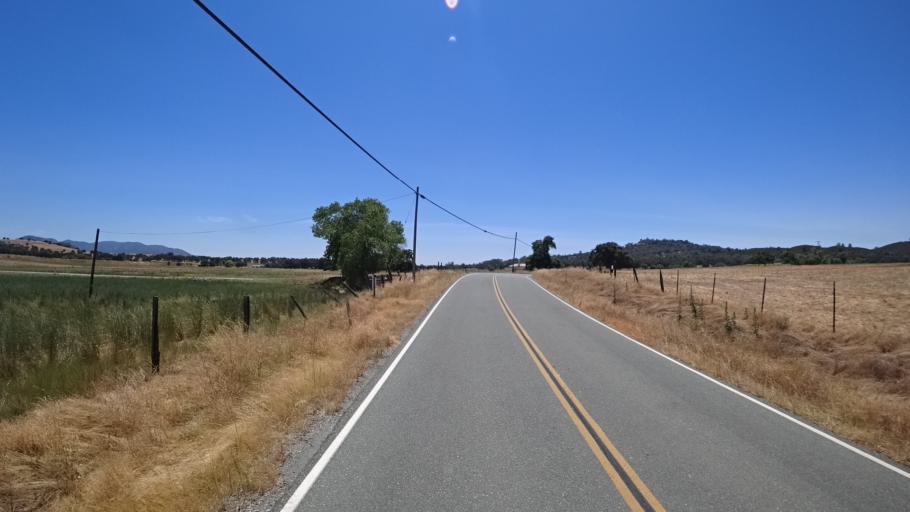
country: US
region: California
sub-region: Calaveras County
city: Valley Springs
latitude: 38.2197
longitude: -120.8235
